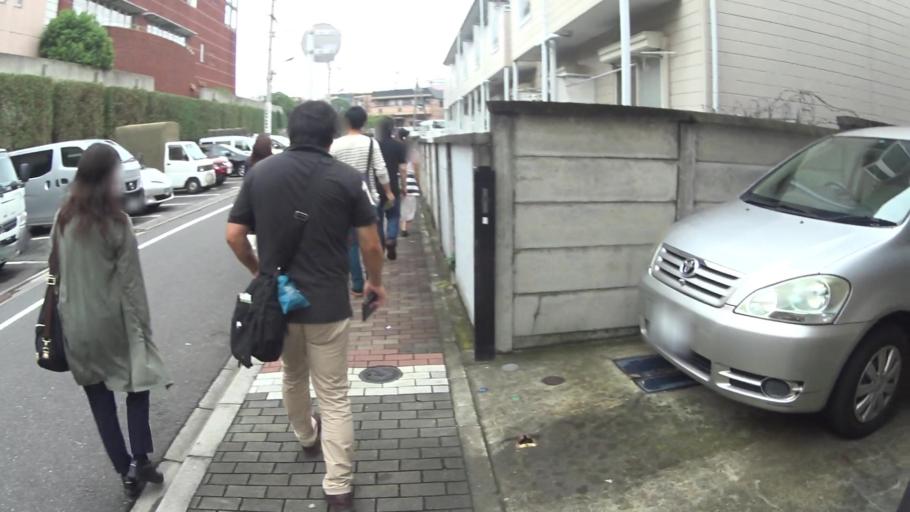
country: JP
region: Tokyo
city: Tokyo
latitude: 35.7390
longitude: 139.6734
